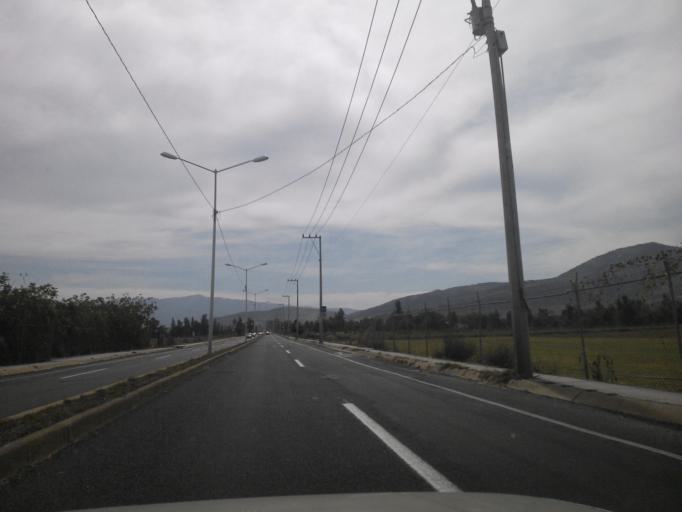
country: MX
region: Jalisco
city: San Sebastian el Grande
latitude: 20.5255
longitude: -103.4082
